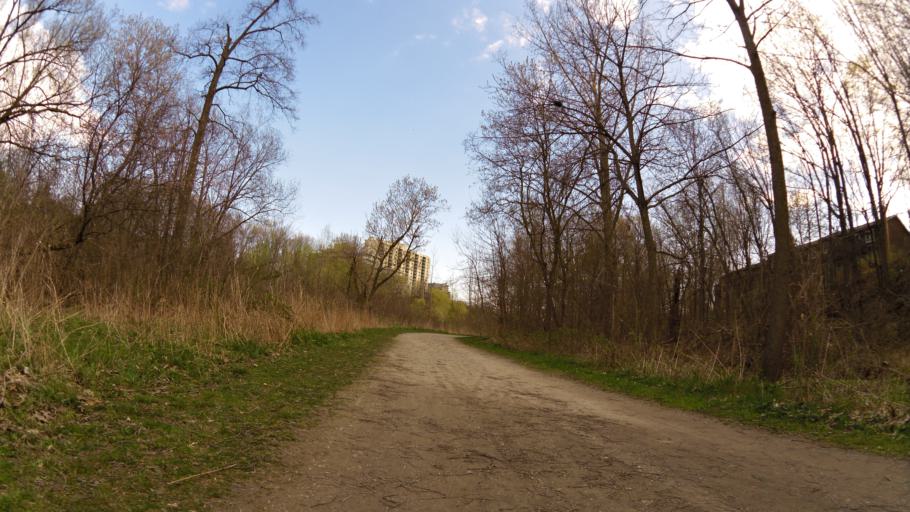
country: CA
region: Ontario
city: Etobicoke
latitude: 43.6422
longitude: -79.5890
